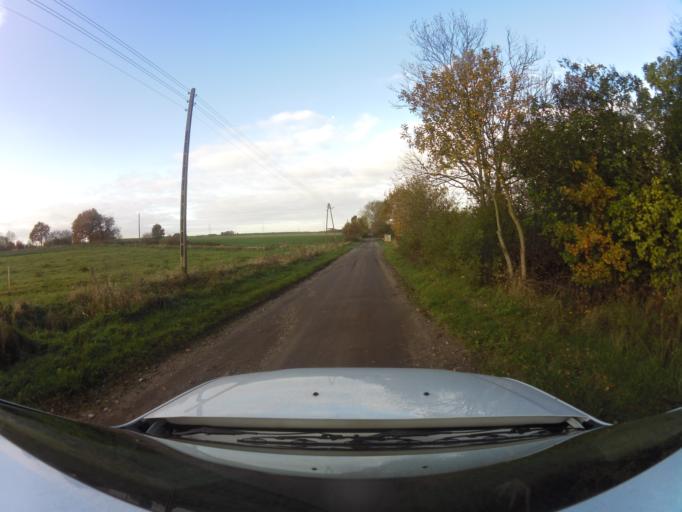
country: PL
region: West Pomeranian Voivodeship
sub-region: Powiat gryficki
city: Trzebiatow
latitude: 54.0494
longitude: 15.2021
